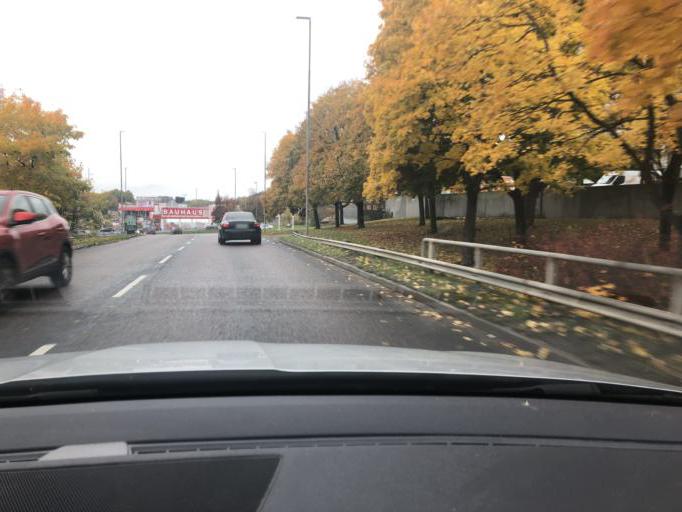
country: SE
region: Stockholm
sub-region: Botkyrka Kommun
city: Alby
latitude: 59.2390
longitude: 17.8407
